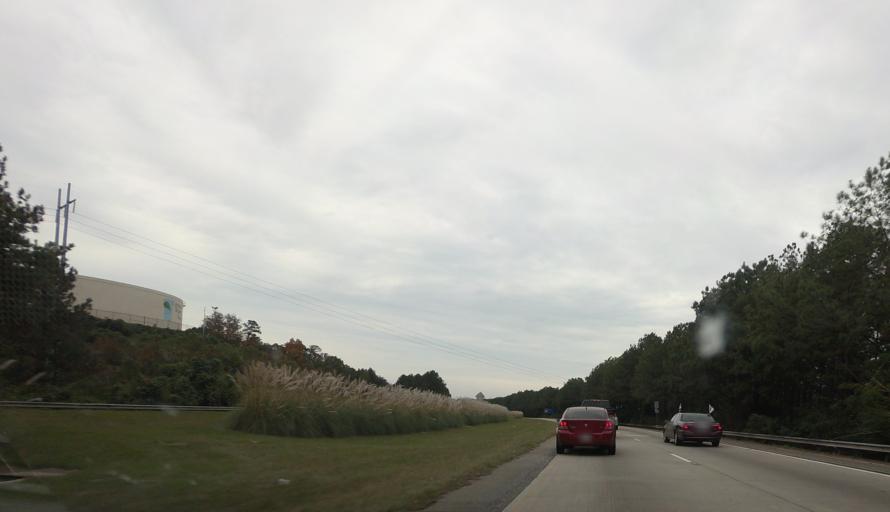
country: US
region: Alabama
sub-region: Russell County
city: Phenix City
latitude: 32.5209
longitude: -84.9904
